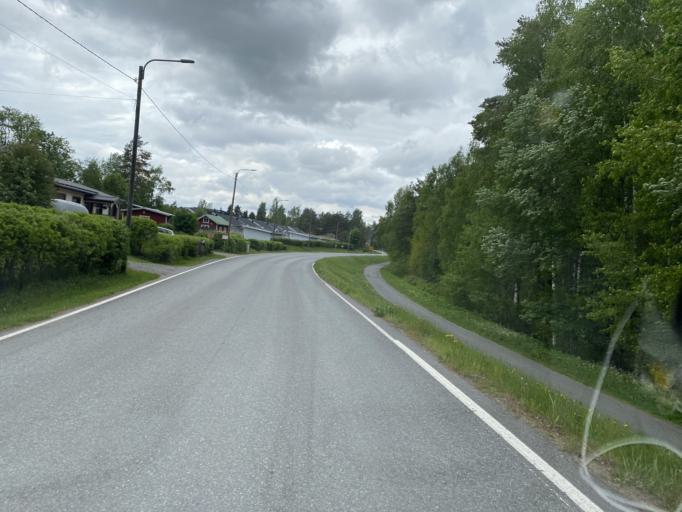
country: FI
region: Pirkanmaa
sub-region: Etelae-Pirkanmaa
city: Urjala
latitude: 61.0771
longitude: 23.5664
